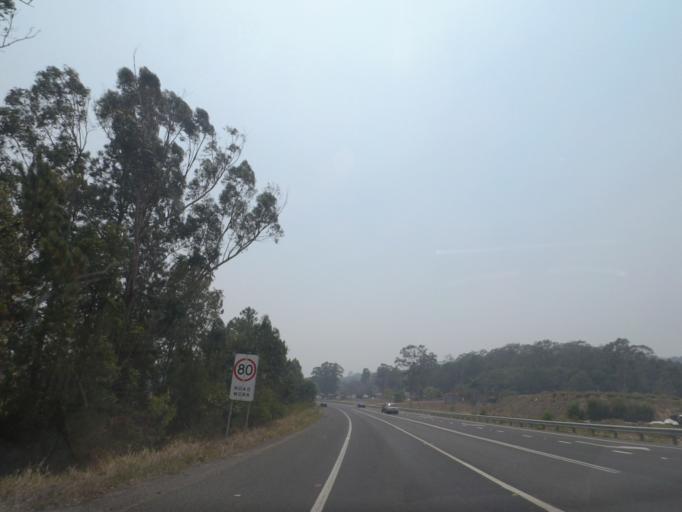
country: AU
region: New South Wales
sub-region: Clarence Valley
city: Maclean
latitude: -29.5634
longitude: 153.1470
